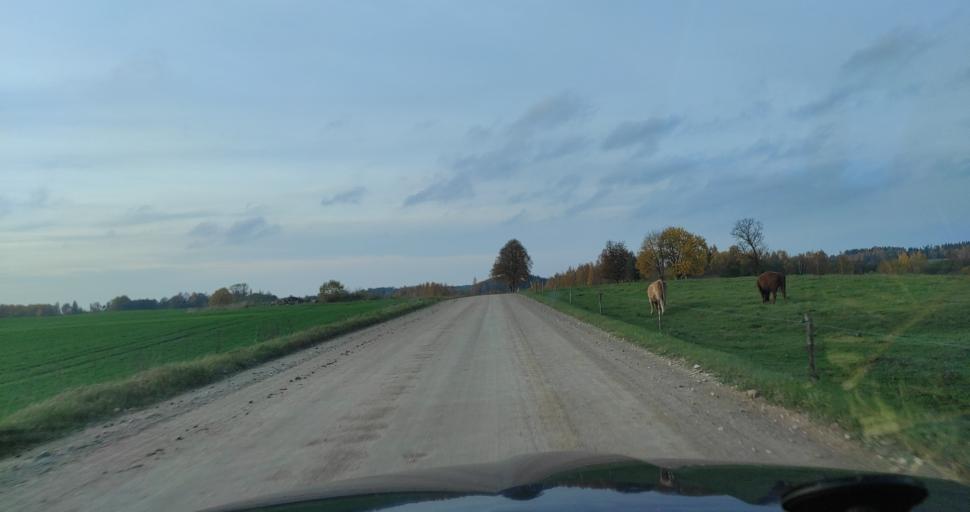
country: LV
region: Skrunda
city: Skrunda
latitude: 56.6413
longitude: 21.8067
